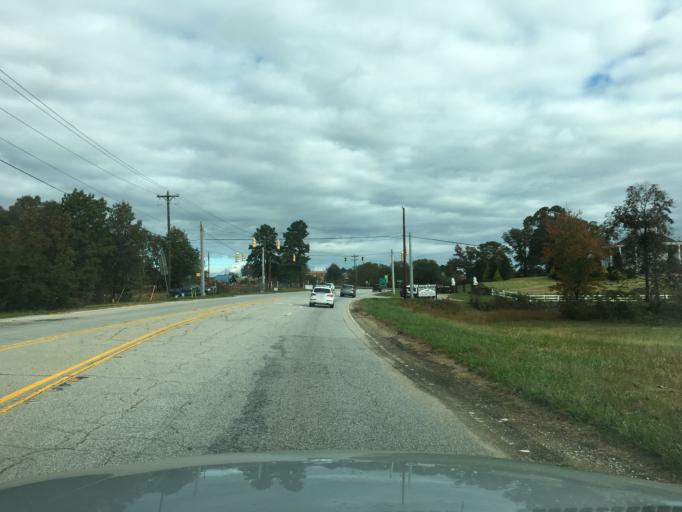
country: US
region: South Carolina
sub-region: Greenville County
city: Tigerville
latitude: 35.0418
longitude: -82.2669
